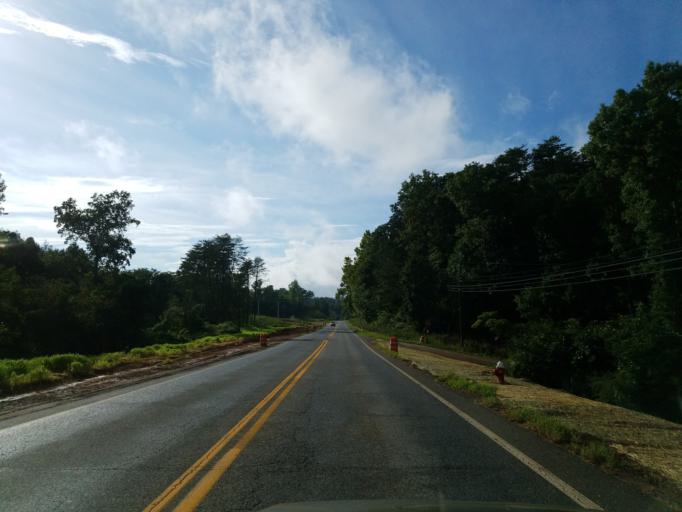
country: US
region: Georgia
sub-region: White County
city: Cleveland
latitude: 34.6091
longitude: -83.7725
